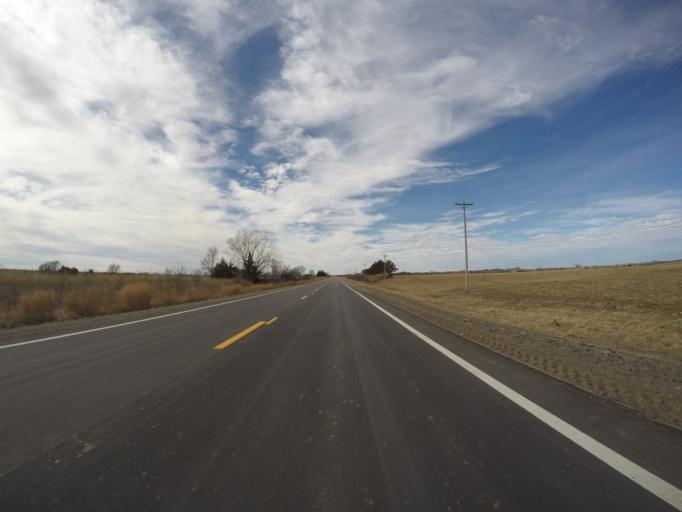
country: US
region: Nebraska
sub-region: Franklin County
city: Franklin
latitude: 40.0965
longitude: -98.8335
